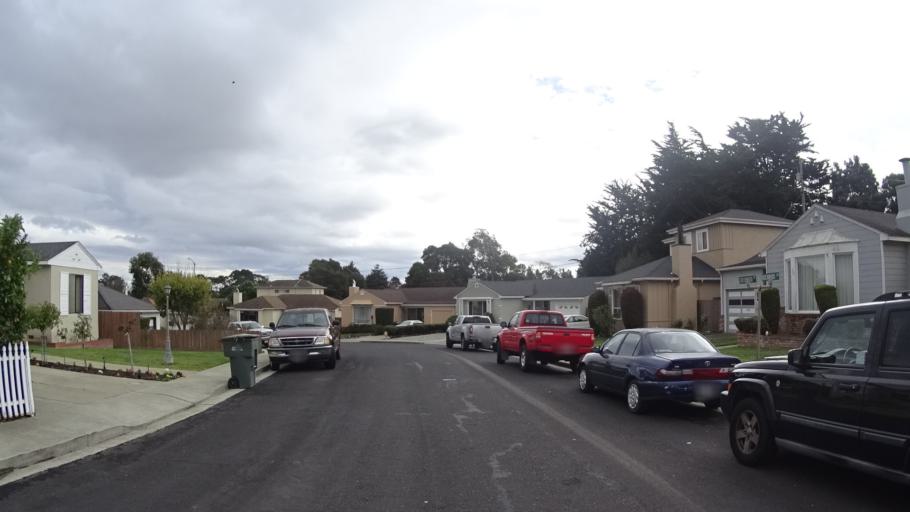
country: US
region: California
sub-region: San Mateo County
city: San Bruno
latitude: 37.6352
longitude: -122.4333
